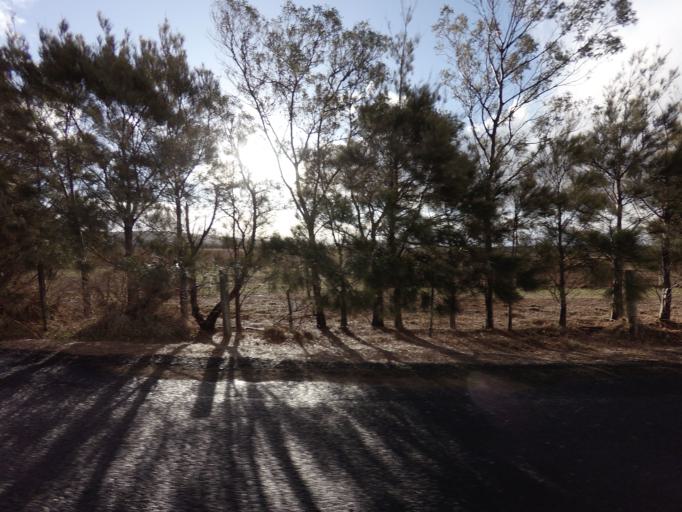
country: AU
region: Tasmania
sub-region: Break O'Day
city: St Helens
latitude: -42.0973
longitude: 148.0677
